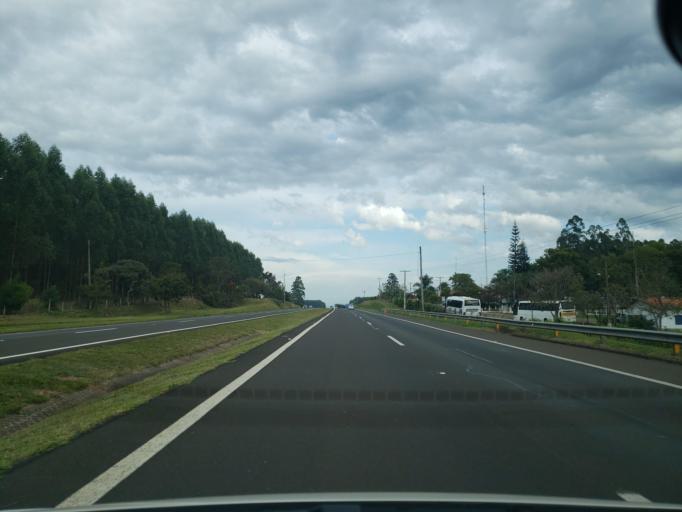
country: BR
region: Sao Paulo
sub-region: Itirapina
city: Itirapina
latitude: -22.2597
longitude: -47.8763
